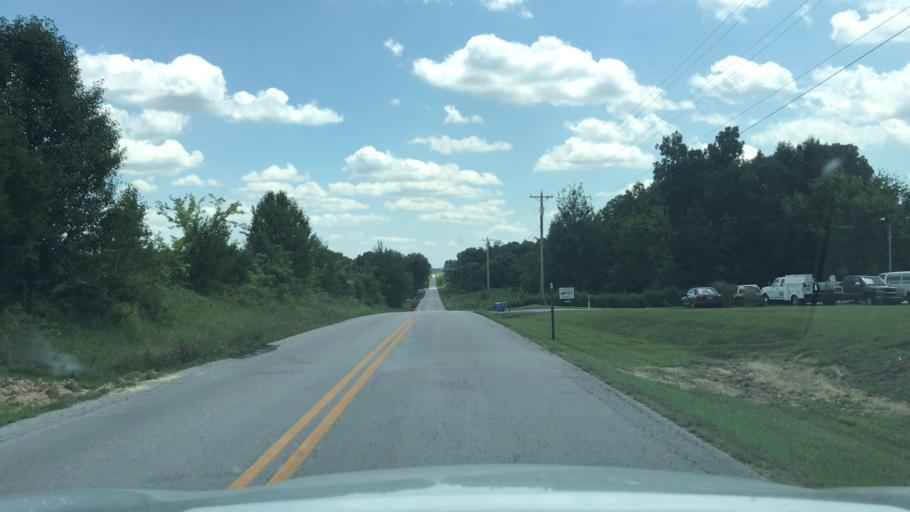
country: US
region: Kentucky
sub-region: Christian County
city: Hopkinsville
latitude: 37.0016
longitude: -87.3676
